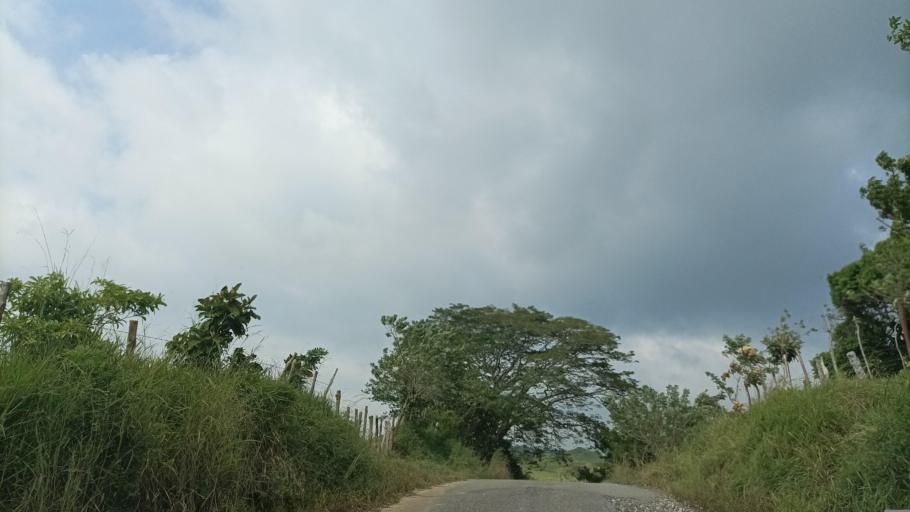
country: MX
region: Veracruz
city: Allende
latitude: 18.1078
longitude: -94.2931
